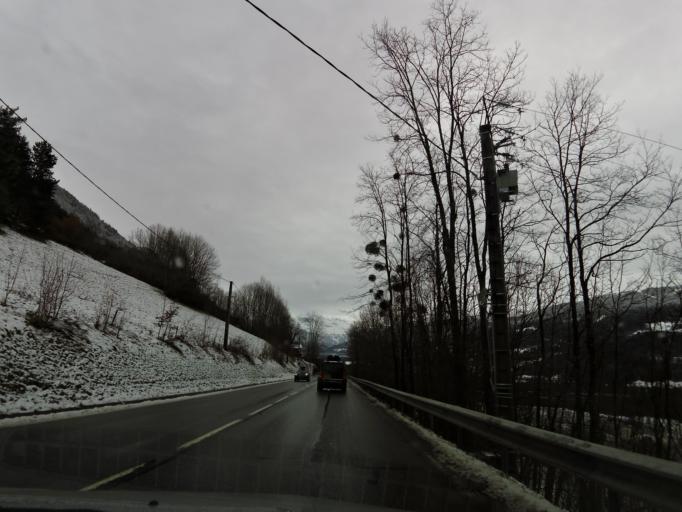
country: FR
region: Rhone-Alpes
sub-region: Departement de la Haute-Savoie
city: Taninges
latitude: 46.1108
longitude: 6.6125
